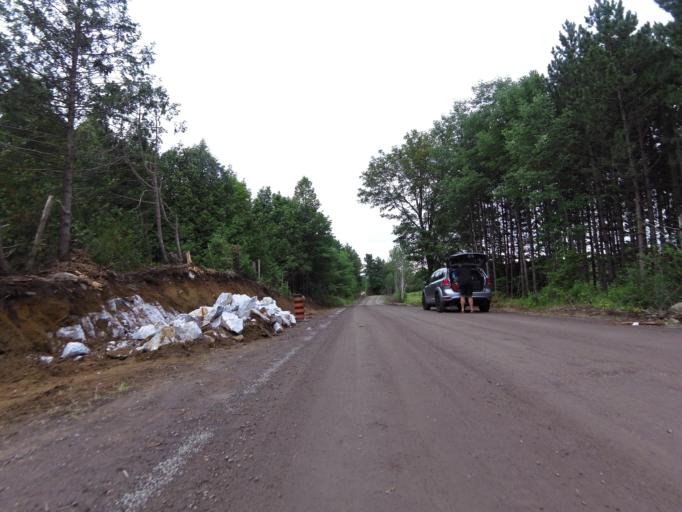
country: CA
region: Ontario
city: Kingston
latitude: 44.5785
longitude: -76.6332
